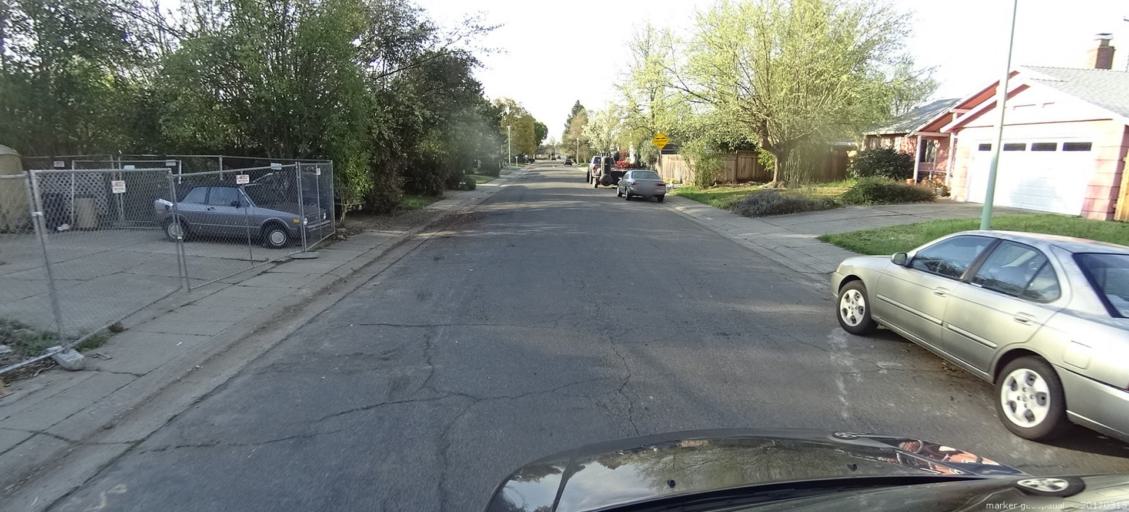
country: US
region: California
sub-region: Sacramento County
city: Parkway
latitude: 38.5166
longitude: -121.5070
